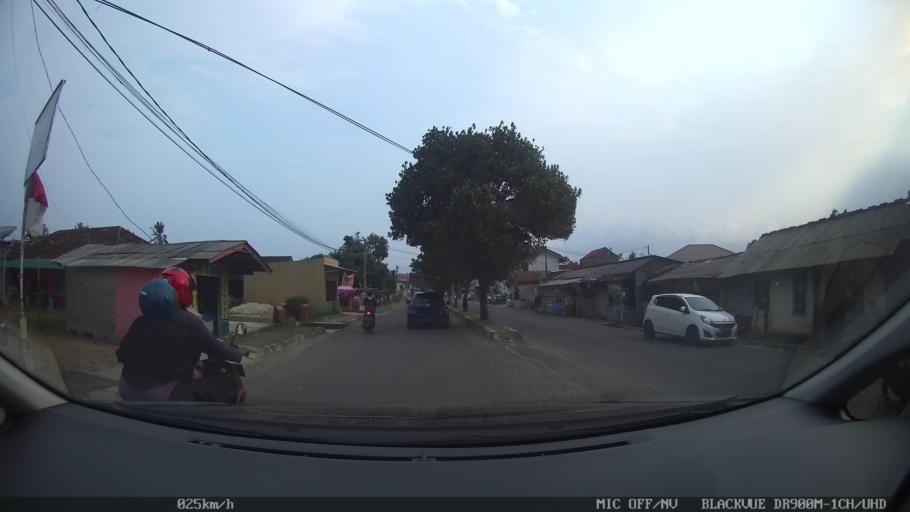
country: ID
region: Lampung
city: Kedaton
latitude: -5.3631
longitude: 105.2352
